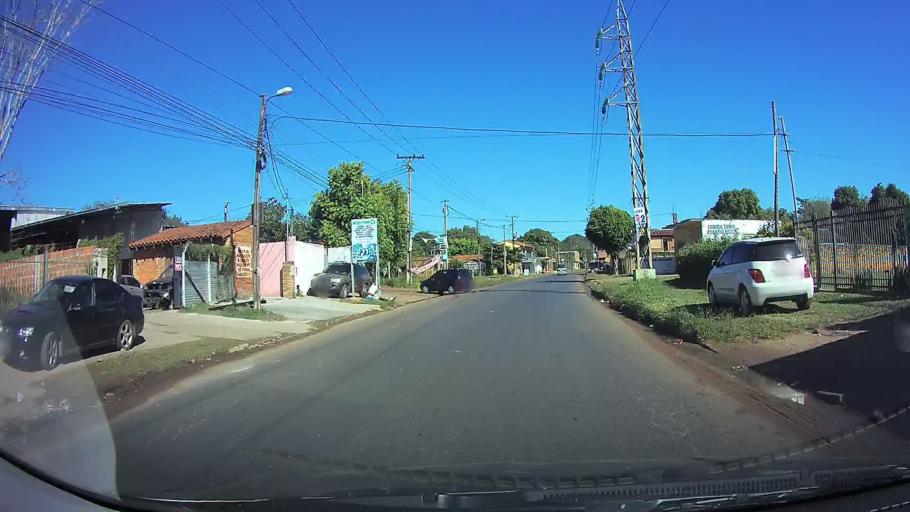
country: PY
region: Central
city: Fernando de la Mora
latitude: -25.3562
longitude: -57.5440
